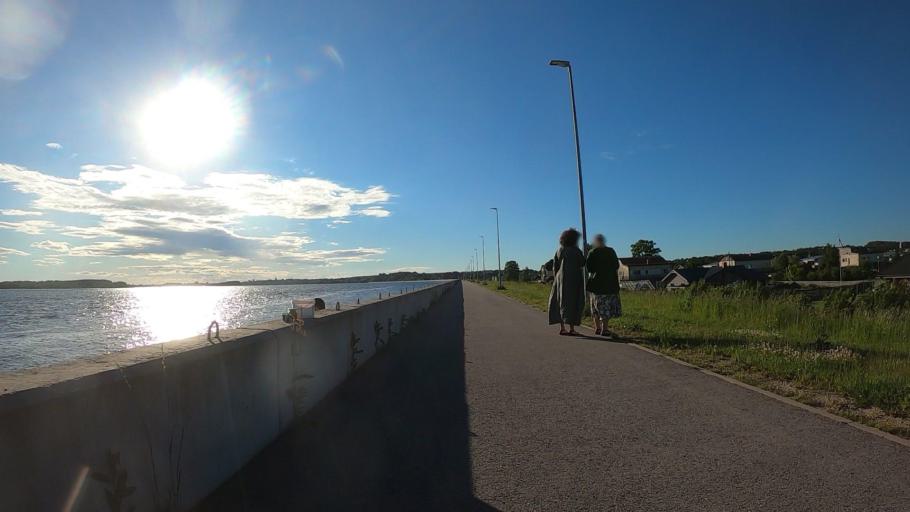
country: LV
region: Ikskile
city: Ikskile
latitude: 56.8339
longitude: 24.4736
